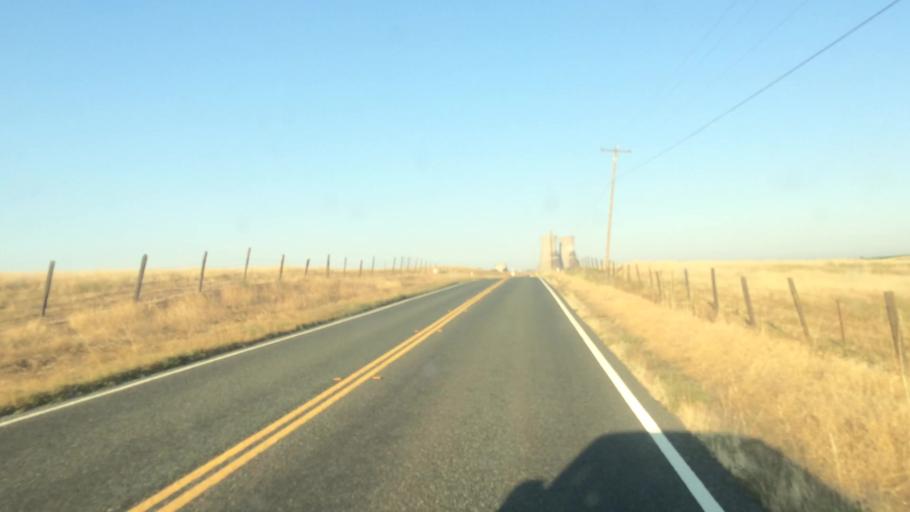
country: US
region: California
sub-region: Sacramento County
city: Clay
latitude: 38.3485
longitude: -121.0909
